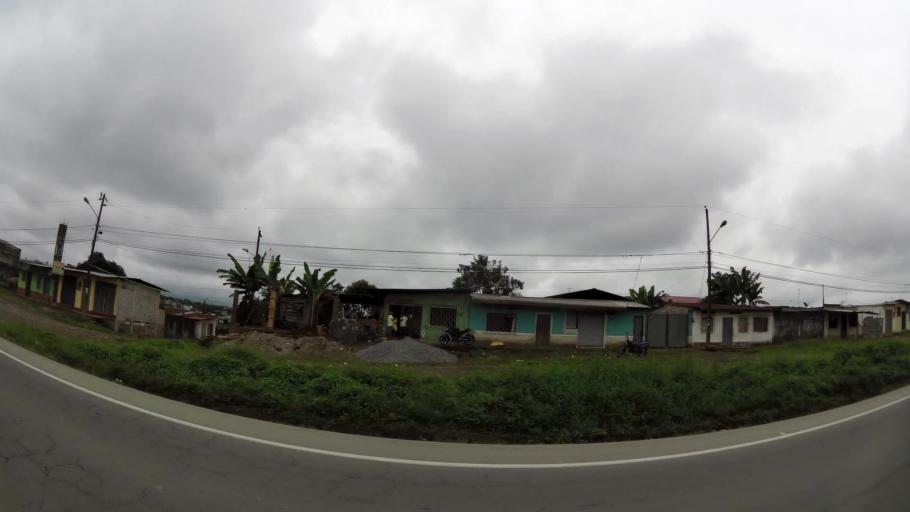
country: EC
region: Santo Domingo de los Tsachilas
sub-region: Canton Santo Domingo de los Colorados
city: Santo Domingo de los Colorados
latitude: -0.2811
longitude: -79.1813
